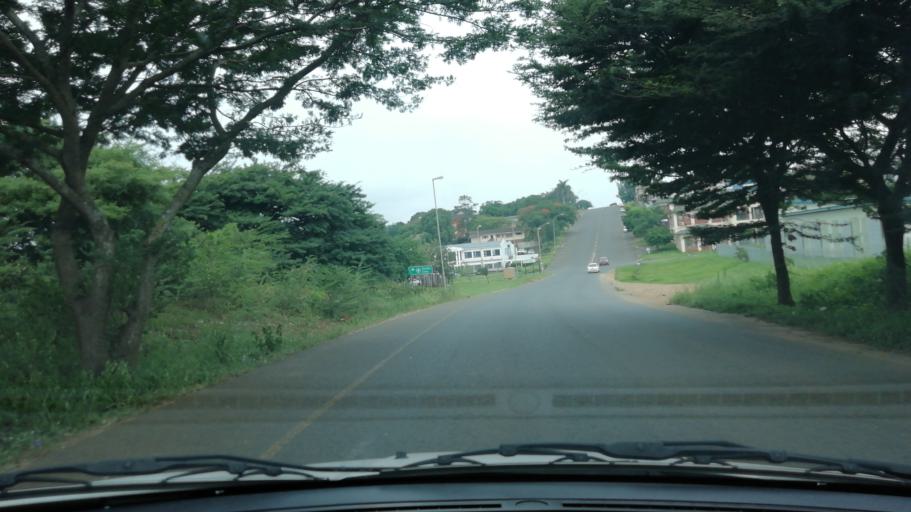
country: ZA
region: KwaZulu-Natal
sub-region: uThungulu District Municipality
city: Empangeni
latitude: -28.7363
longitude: 31.8920
